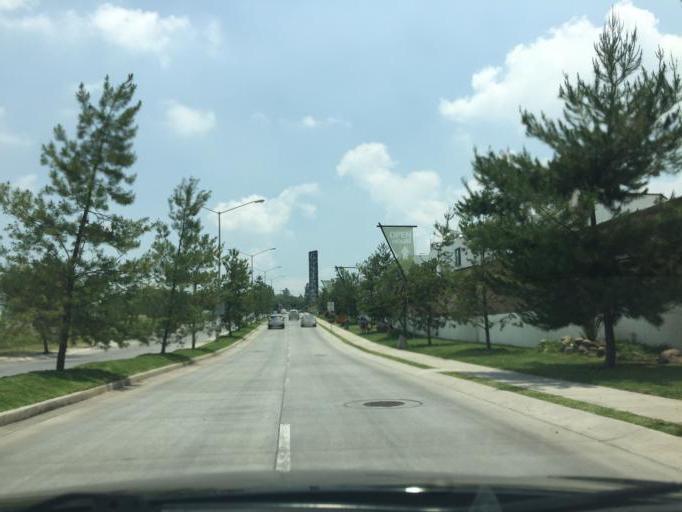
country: MX
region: Guanajuato
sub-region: Leon
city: La Ermita
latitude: 21.1705
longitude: -101.7341
